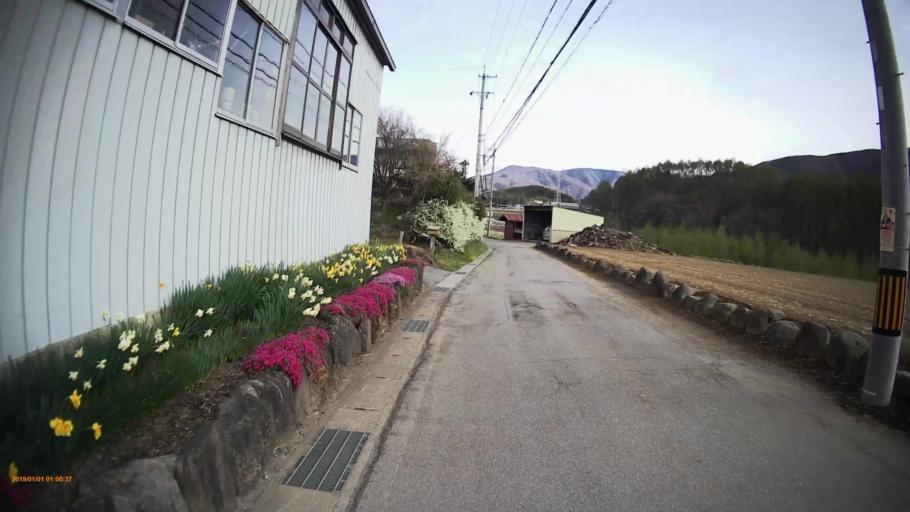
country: JP
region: Nagano
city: Chino
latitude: 35.9200
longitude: 138.2156
